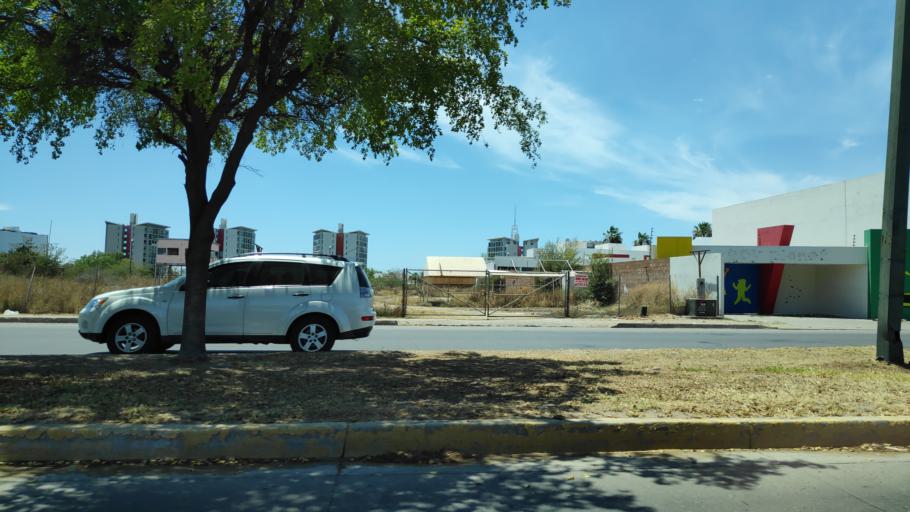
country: MX
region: Sinaloa
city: Culiacan
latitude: 24.8251
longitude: -107.3999
